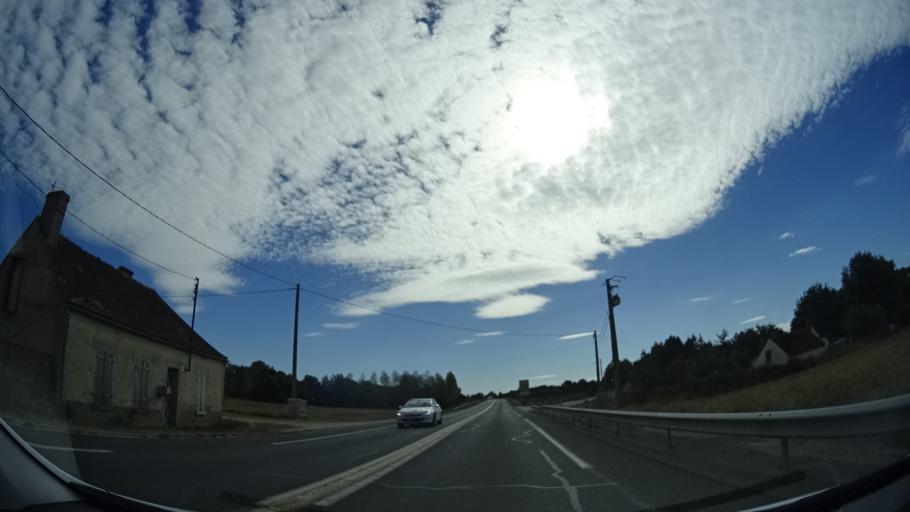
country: FR
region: Centre
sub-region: Departement du Loiret
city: Bellegarde
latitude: 47.9557
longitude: 2.3841
